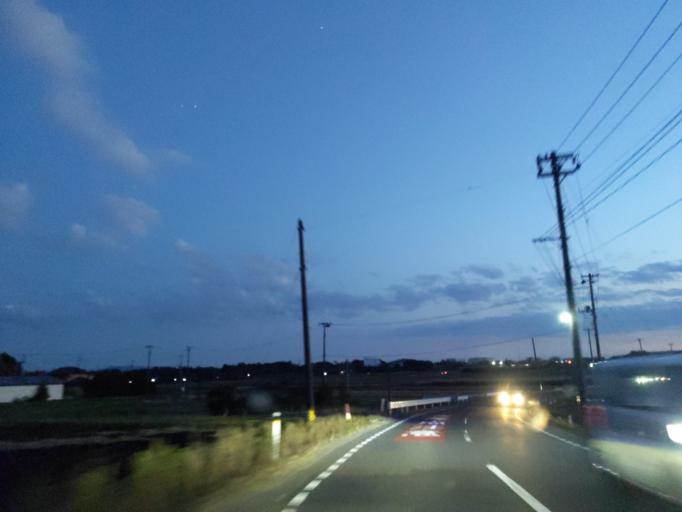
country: JP
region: Fukushima
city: Koriyama
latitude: 37.4316
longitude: 140.3146
